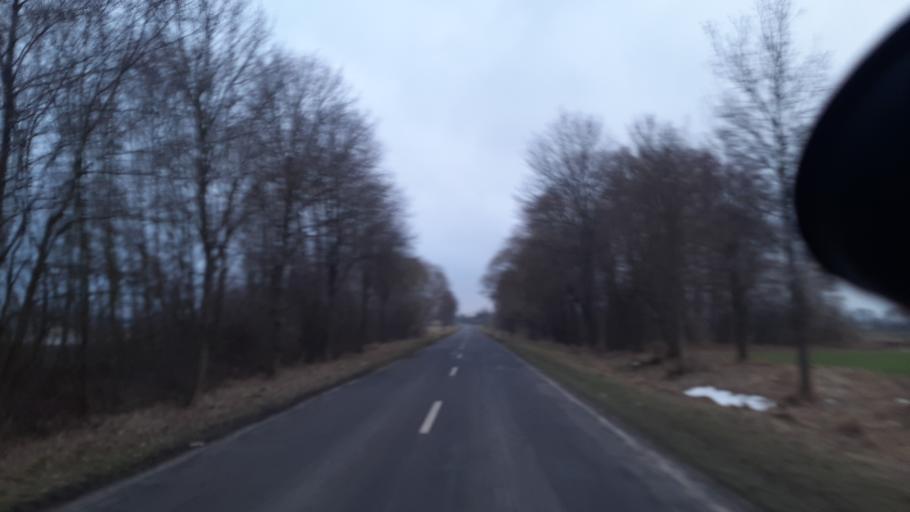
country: PL
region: Lublin Voivodeship
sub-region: Powiat parczewski
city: Debowa Kloda
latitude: 51.6185
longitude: 23.0996
